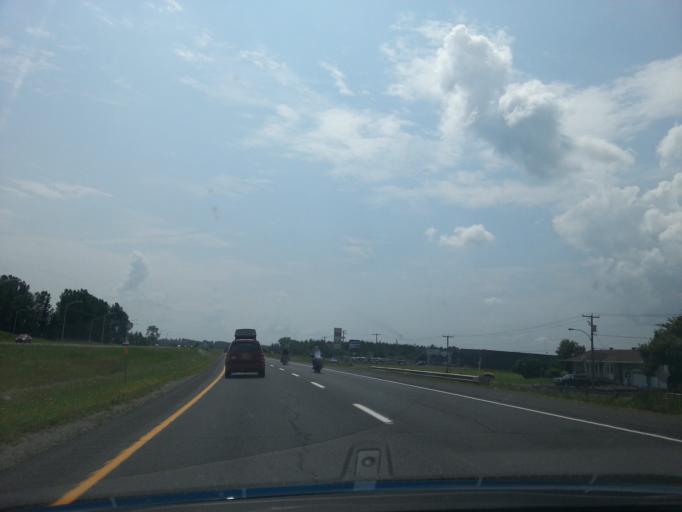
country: CA
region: Quebec
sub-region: Chaudiere-Appalaches
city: Saint-Antoine-de-Tilly
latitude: 46.5381
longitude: -71.6392
